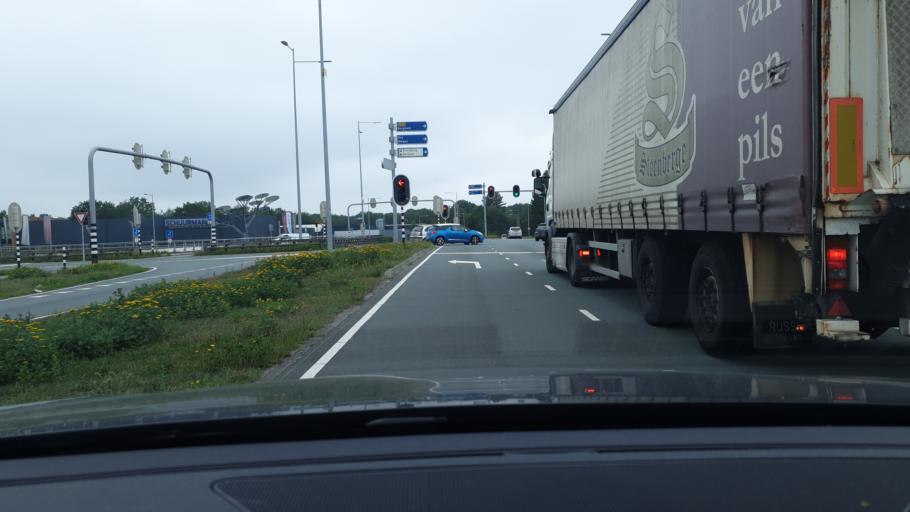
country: NL
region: North Brabant
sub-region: Gemeente Oss
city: Berghem
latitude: 51.7565
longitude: 5.5572
